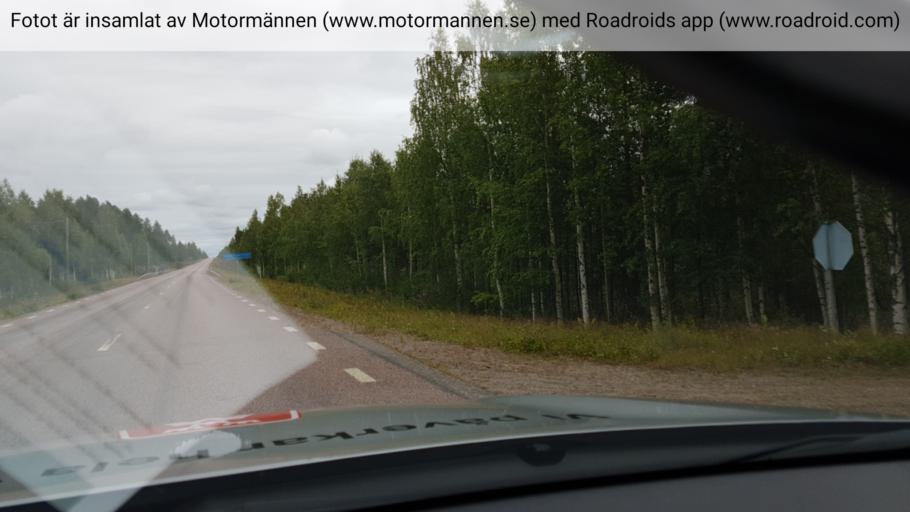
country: SE
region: Norrbotten
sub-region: Overkalix Kommun
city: OEverkalix
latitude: 67.0791
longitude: 22.5367
